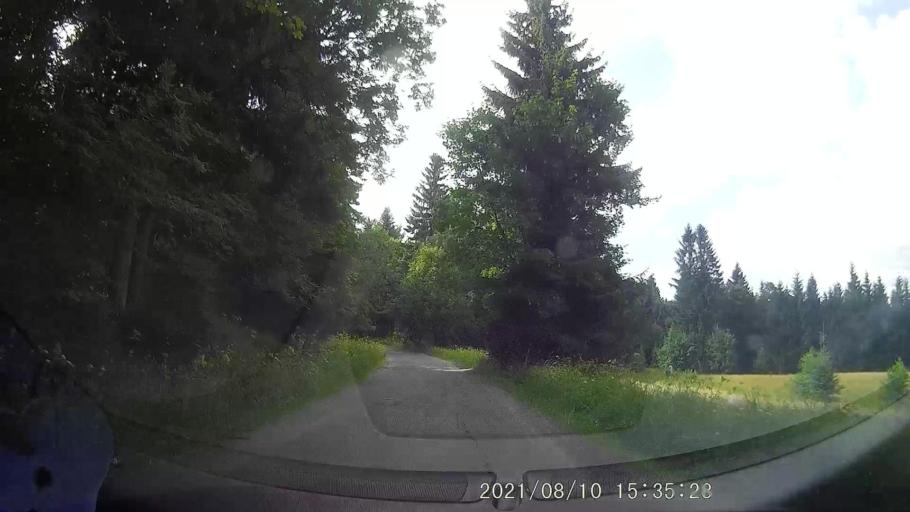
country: PL
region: Lower Silesian Voivodeship
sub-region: Powiat klodzki
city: Radkow
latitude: 50.4871
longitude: 16.3488
